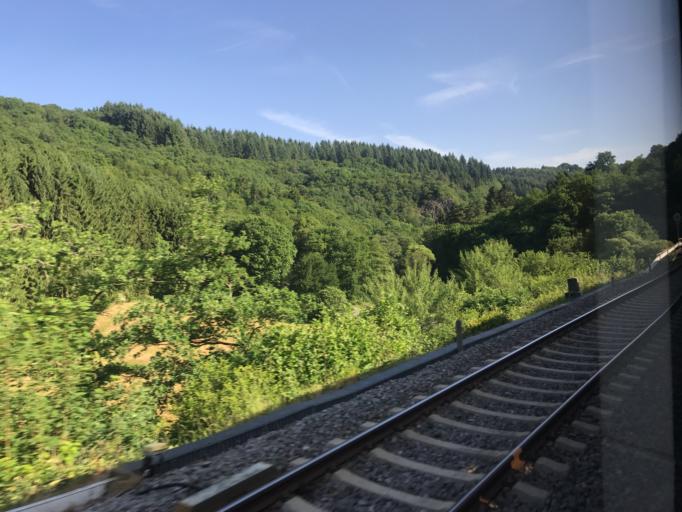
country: DE
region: Rheinland-Pfalz
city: Frauenberg
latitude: 49.6633
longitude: 7.2709
